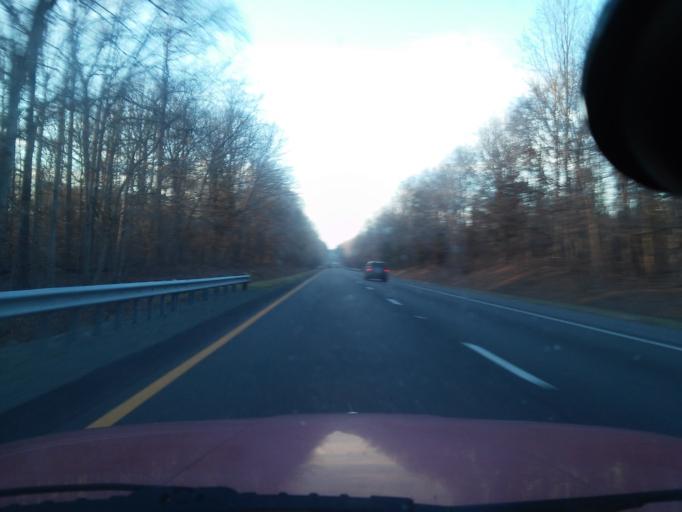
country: US
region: Virginia
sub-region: Goochland County
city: Goochland
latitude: 37.7714
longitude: -77.8762
